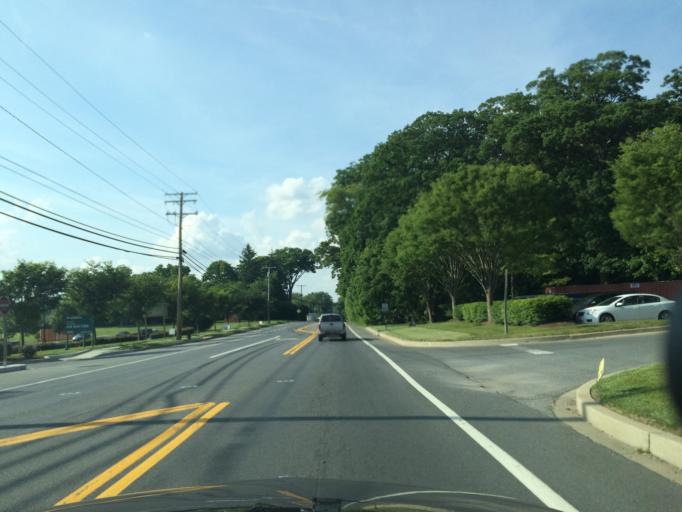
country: US
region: Maryland
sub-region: Carroll County
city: Sykesville
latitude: 39.3031
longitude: -77.0206
